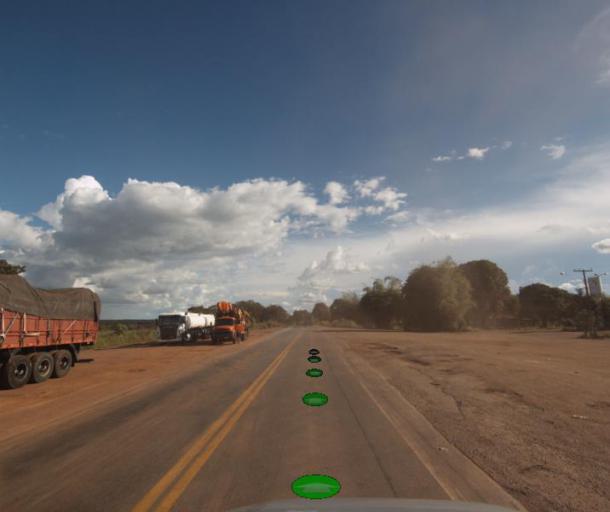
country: BR
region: Goias
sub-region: Porangatu
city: Porangatu
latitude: -13.1086
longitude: -49.2013
